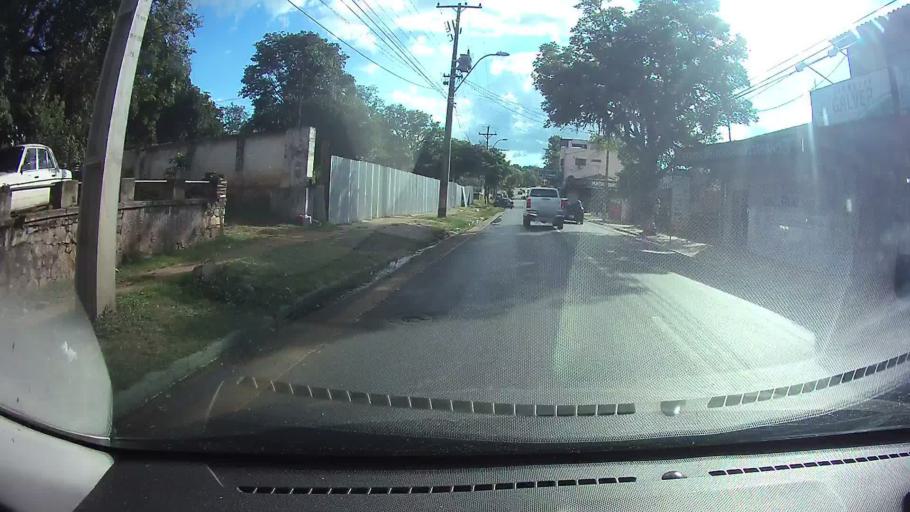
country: PY
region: Cordillera
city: Caacupe
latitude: -25.3870
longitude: -57.1450
